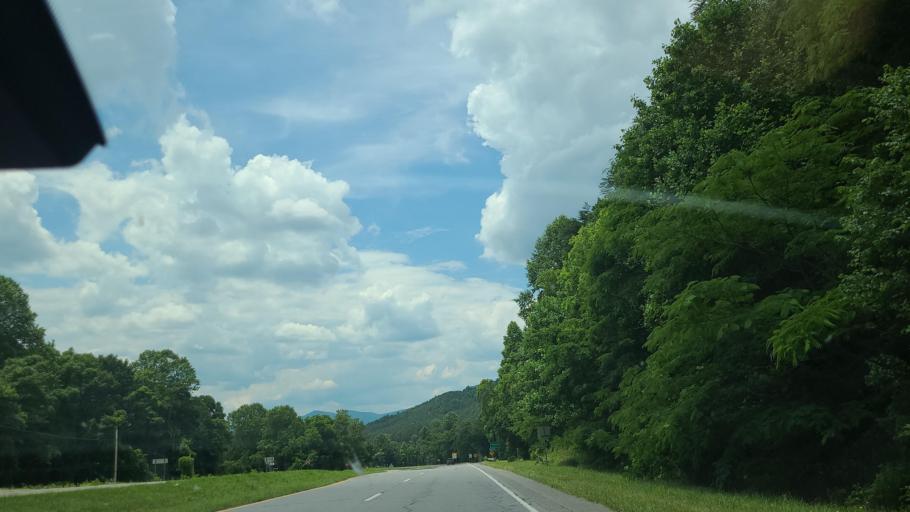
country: US
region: Georgia
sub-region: Fannin County
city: McCaysville
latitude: 35.0213
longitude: -84.3164
